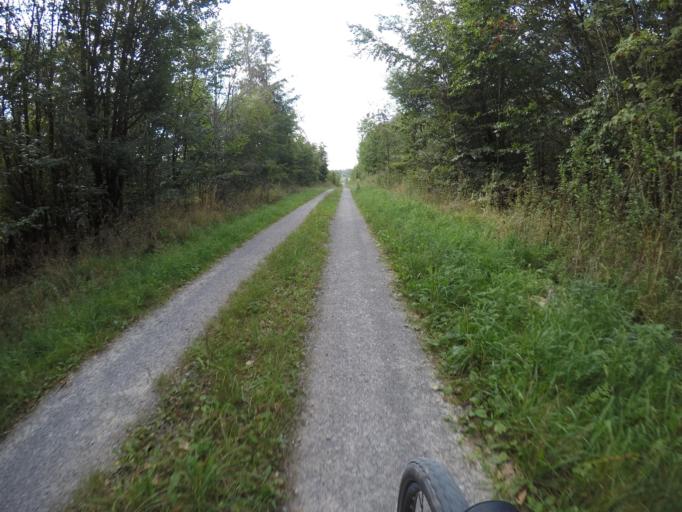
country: DE
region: Baden-Wuerttemberg
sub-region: Karlsruhe Region
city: Gechingen
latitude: 48.6746
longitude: 8.8211
